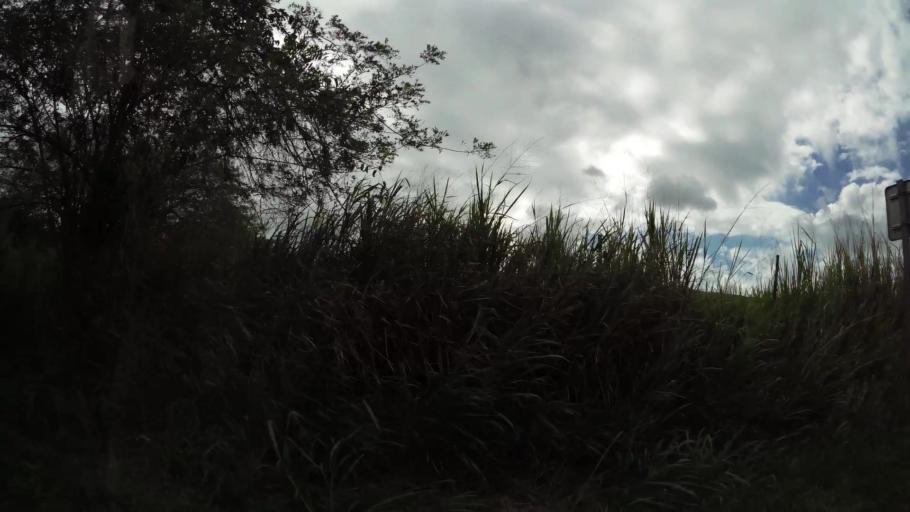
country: GP
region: Guadeloupe
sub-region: Guadeloupe
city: Sainte-Rose
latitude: 16.3248
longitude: -61.7006
